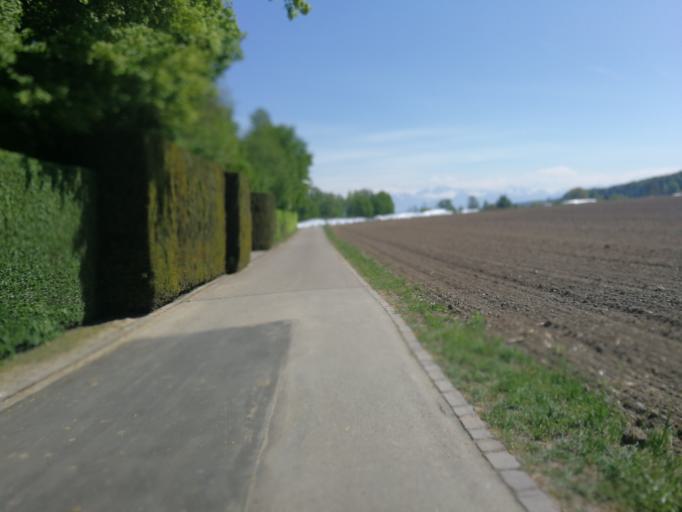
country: CH
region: Zurich
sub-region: Bezirk Uster
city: Fallanden
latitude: 47.3715
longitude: 8.6480
